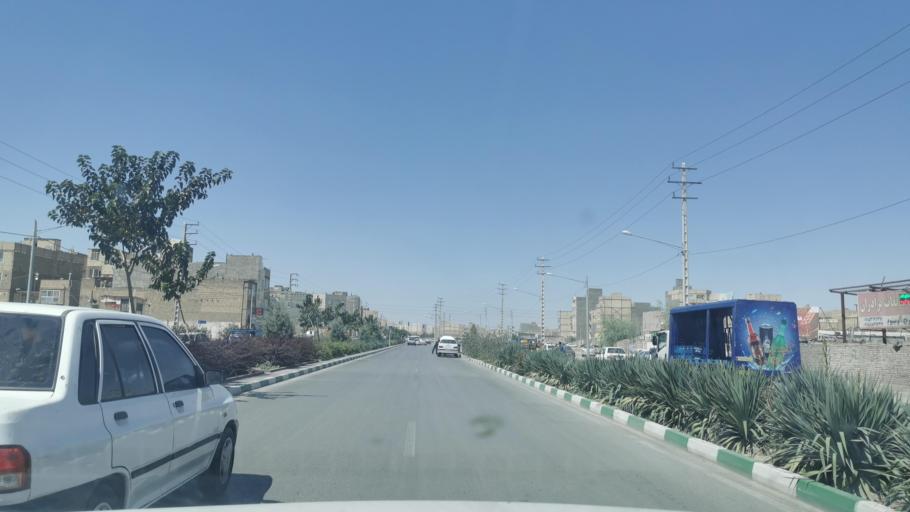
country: IR
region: Razavi Khorasan
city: Mashhad
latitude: 36.3548
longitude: 59.5687
